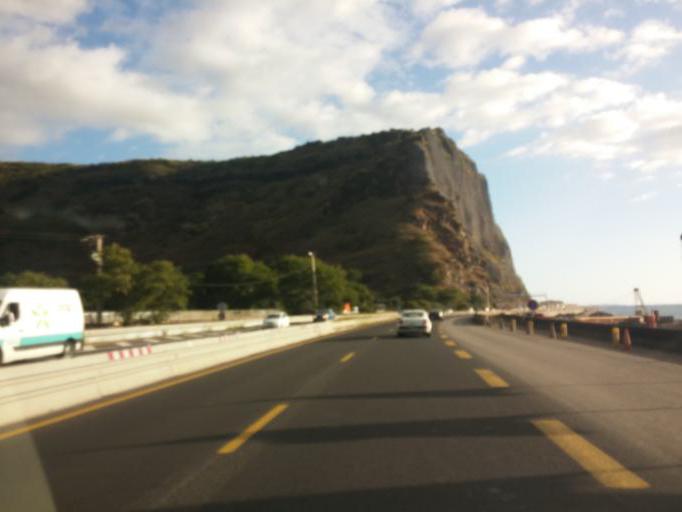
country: RE
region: Reunion
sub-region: Reunion
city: La Possession
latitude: -20.8959
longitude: 55.3764
